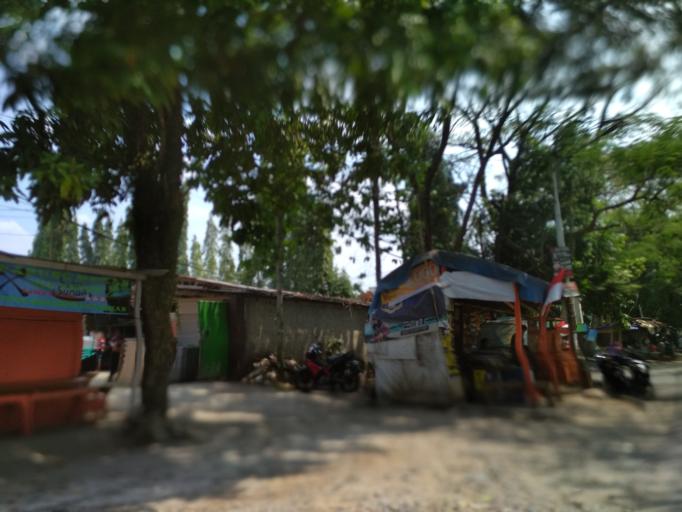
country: ID
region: West Java
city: Bogor
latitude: -6.5674
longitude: 106.7532
